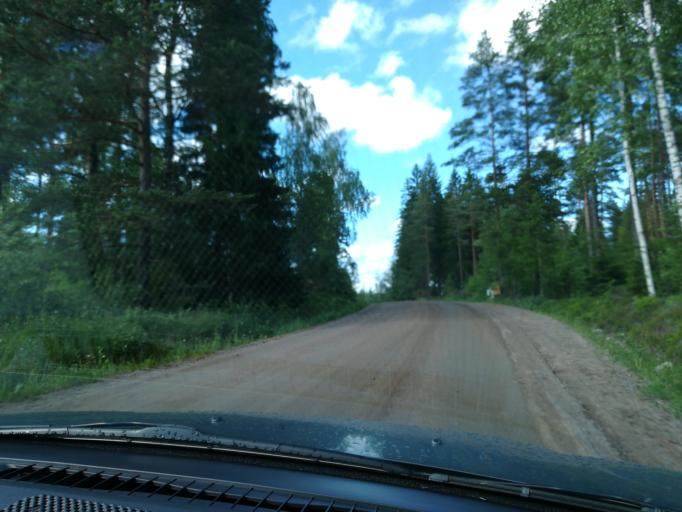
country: FI
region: South Karelia
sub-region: Lappeenranta
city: Savitaipale
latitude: 61.2933
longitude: 27.6567
